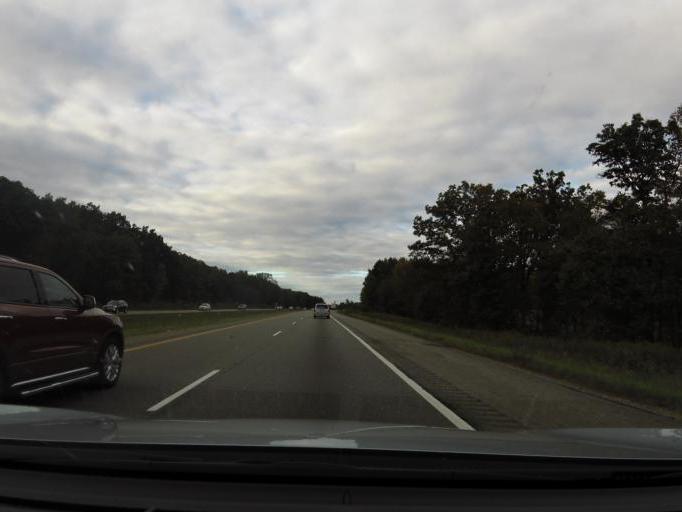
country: US
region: Michigan
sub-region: Livingston County
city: Brighton
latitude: 42.5674
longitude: -83.7407
